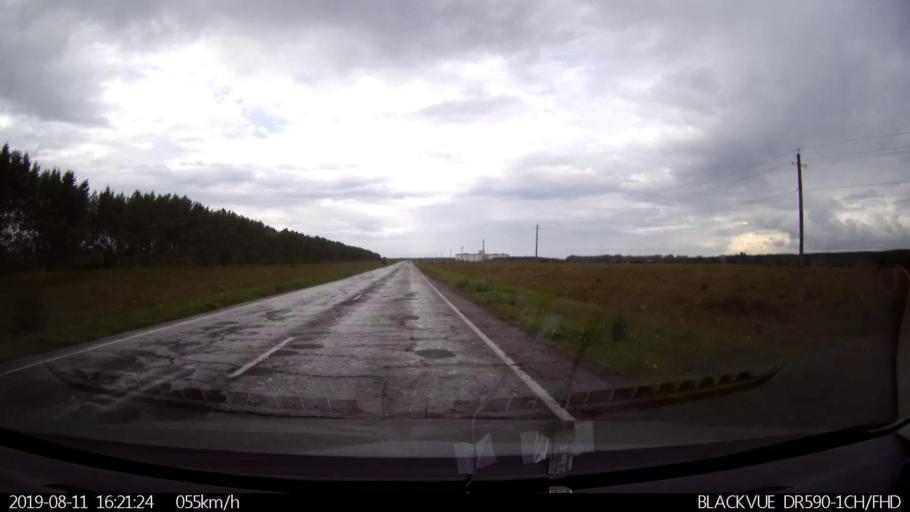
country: RU
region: Ulyanovsk
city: Mayna
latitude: 54.0797
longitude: 47.5981
